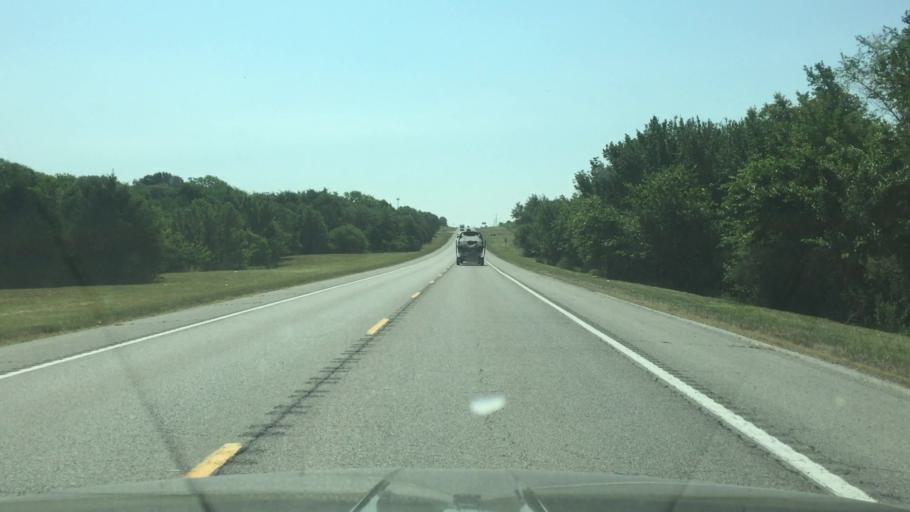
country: US
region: Missouri
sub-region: Pettis County
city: Sedalia
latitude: 38.6892
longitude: -93.0469
